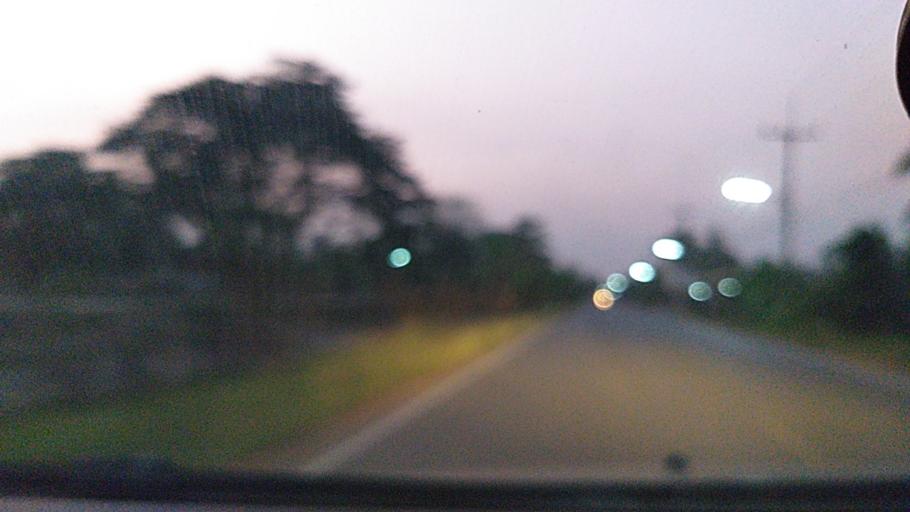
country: TH
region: Sing Buri
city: Sing Buri
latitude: 14.8348
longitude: 100.3983
